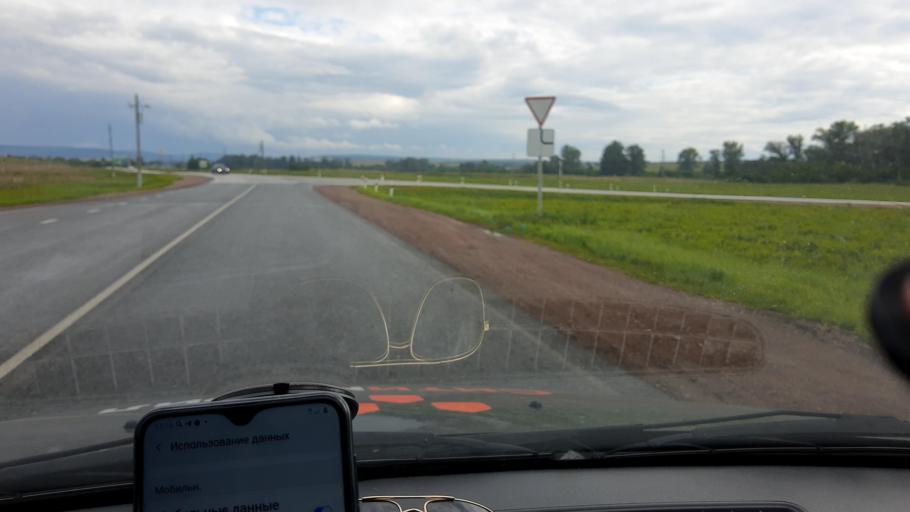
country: RU
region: Bashkortostan
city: Karmaskaly
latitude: 53.9311
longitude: 56.4212
